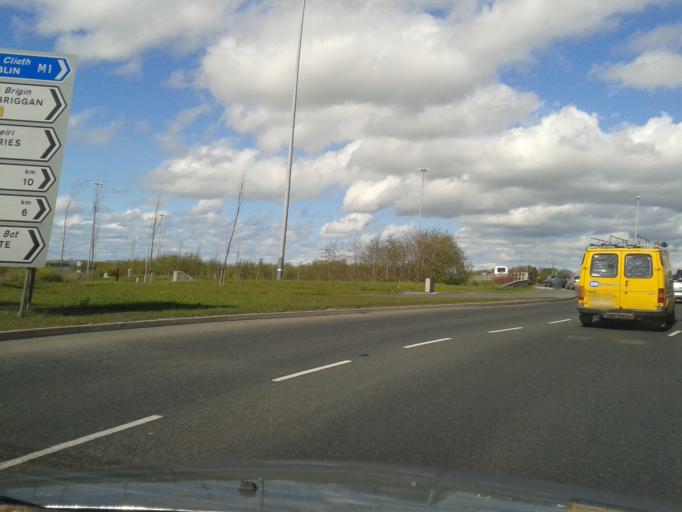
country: IE
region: Leinster
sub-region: Fingal County
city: Swords
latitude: 53.4772
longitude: -6.2063
